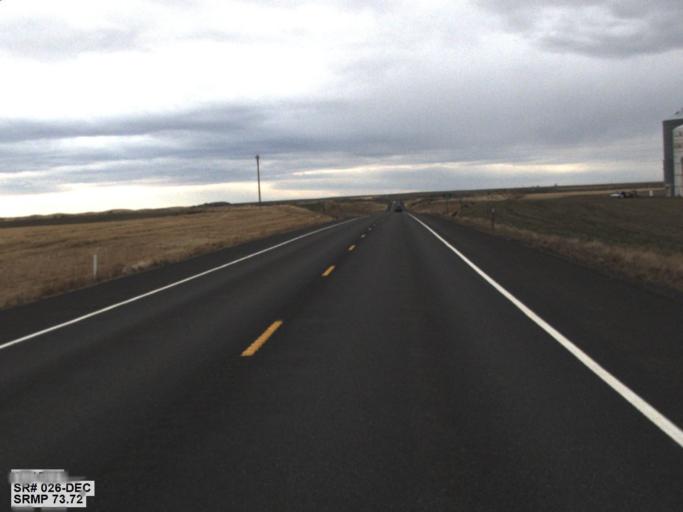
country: US
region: Washington
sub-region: Adams County
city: Ritzville
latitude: 46.7955
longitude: -118.4818
